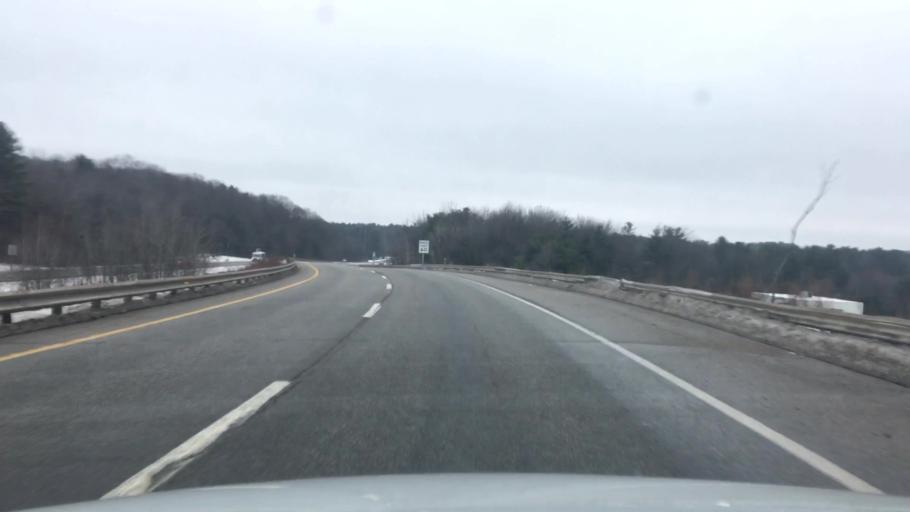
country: US
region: Maine
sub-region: Cumberland County
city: Scarborough
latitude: 43.6043
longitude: -70.3184
